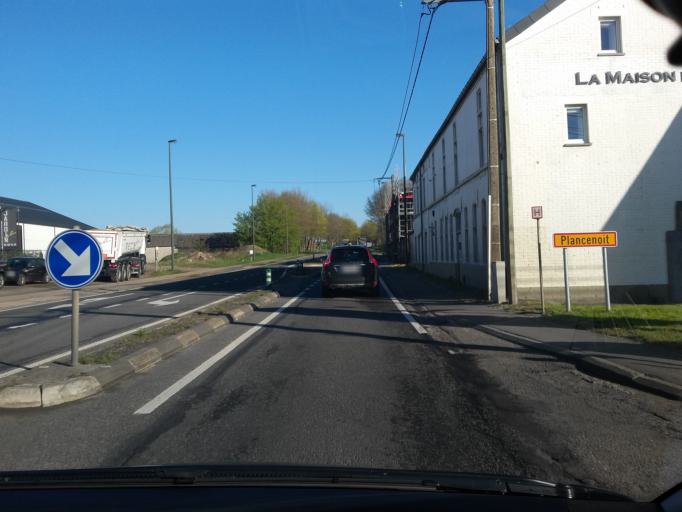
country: BE
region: Wallonia
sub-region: Province du Brabant Wallon
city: Genappe
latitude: 50.6514
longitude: 4.4157
